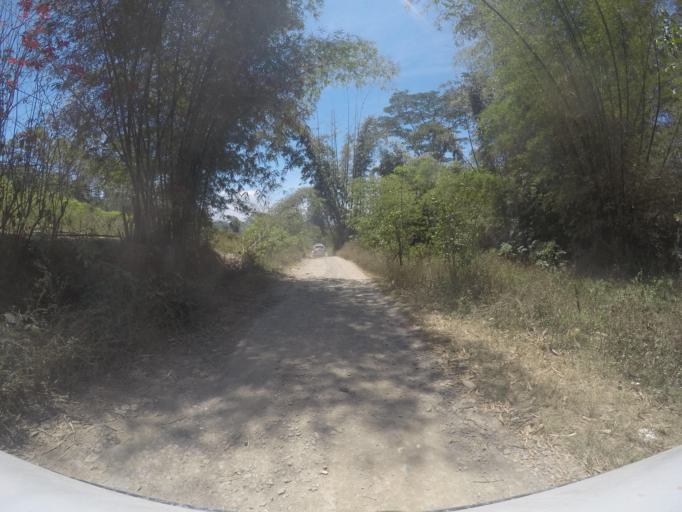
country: TL
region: Ermera
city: Gleno
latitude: -8.7335
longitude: 125.4124
